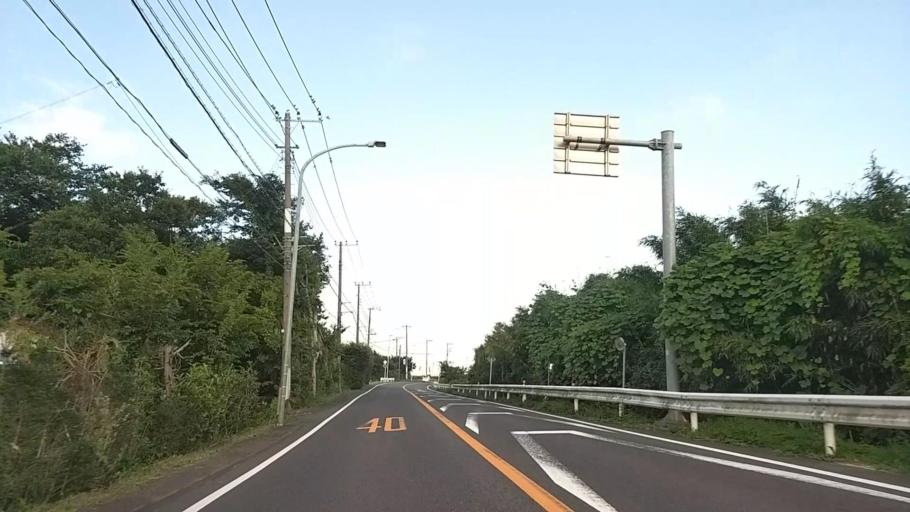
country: JP
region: Kanagawa
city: Isehara
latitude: 35.3564
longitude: 139.3061
